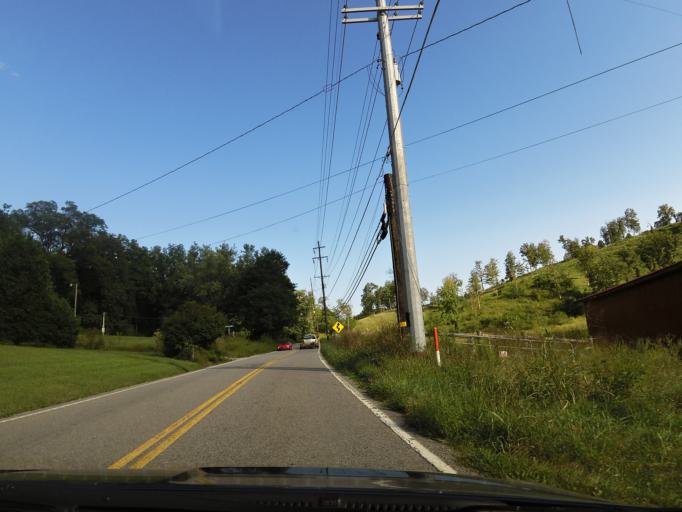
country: US
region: Tennessee
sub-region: Union County
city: Maynardville
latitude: 36.2555
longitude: -83.7661
